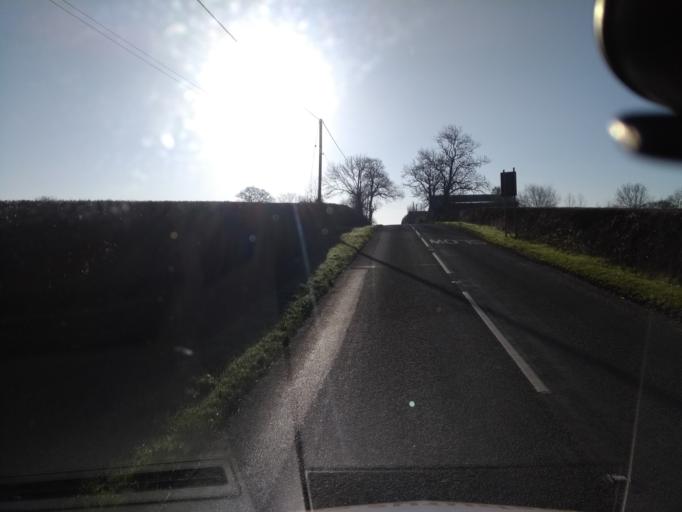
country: GB
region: England
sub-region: Somerset
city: Wincanton
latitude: 51.0753
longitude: -2.3789
